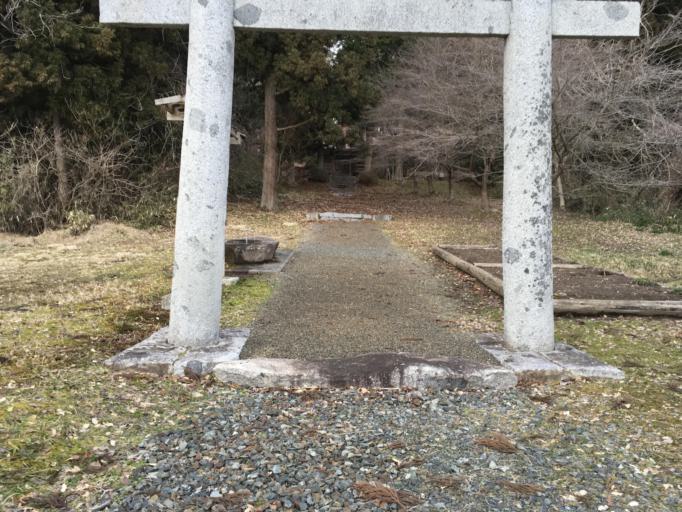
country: JP
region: Iwate
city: Kitakami
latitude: 39.2265
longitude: 141.2286
